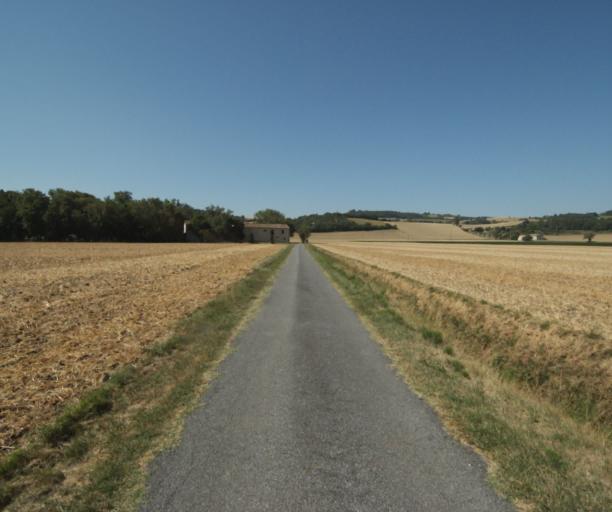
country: FR
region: Midi-Pyrenees
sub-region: Departement du Tarn
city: Puylaurens
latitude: 43.5213
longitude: 1.9526
